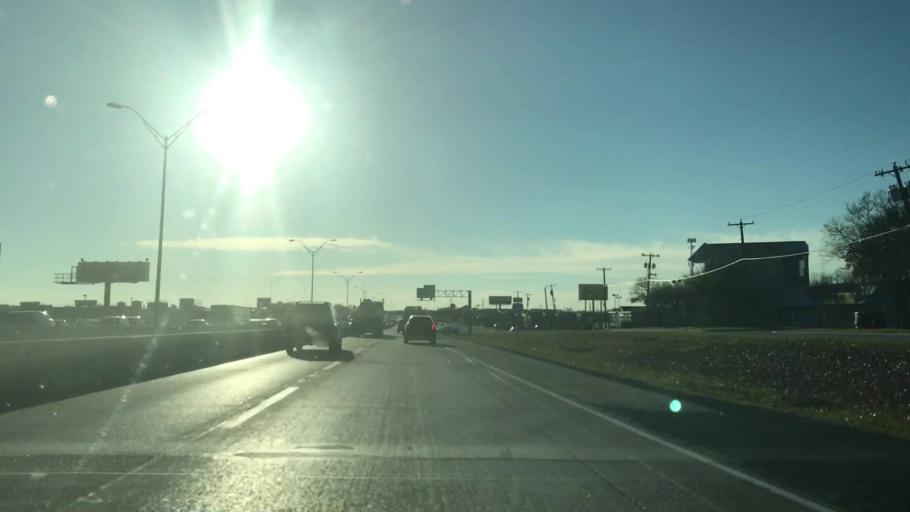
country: US
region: Texas
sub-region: Dallas County
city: Mesquite
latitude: 32.8069
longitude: -96.6620
